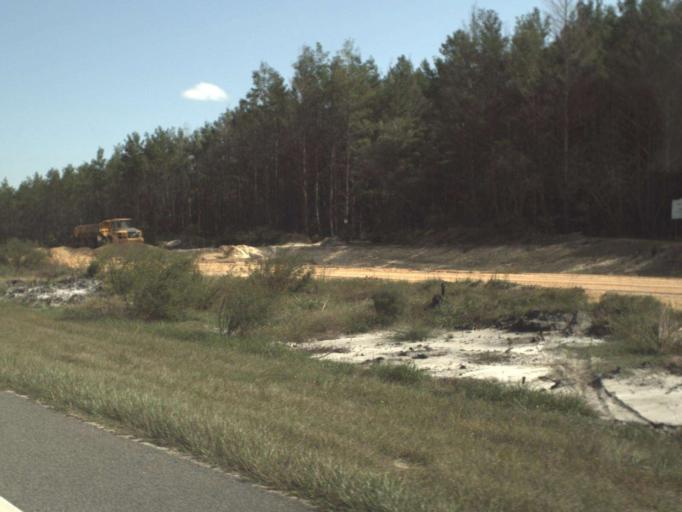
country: US
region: Florida
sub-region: Walton County
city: Freeport
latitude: 30.5084
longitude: -86.1140
